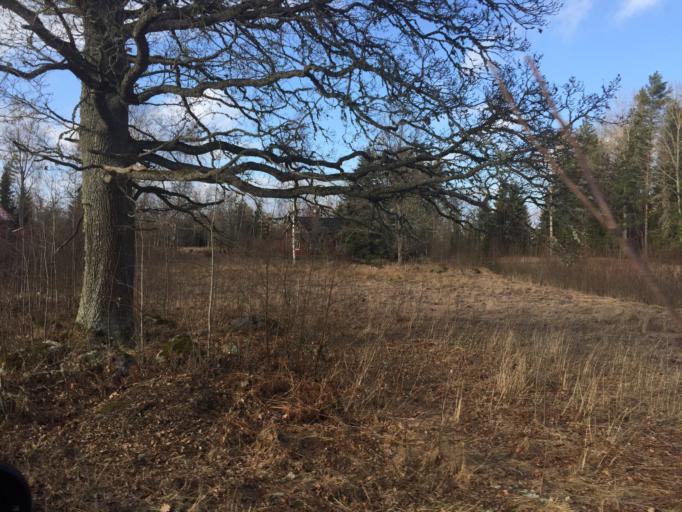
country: SE
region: Soedermanland
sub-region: Vingakers Kommun
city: Vingaker
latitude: 59.0121
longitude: 15.8013
